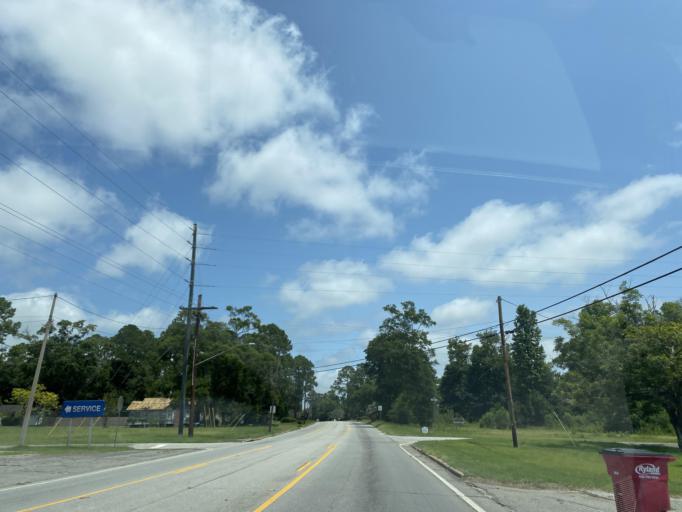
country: US
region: Georgia
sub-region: Telfair County
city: McRae
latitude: 32.0587
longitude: -82.9043
